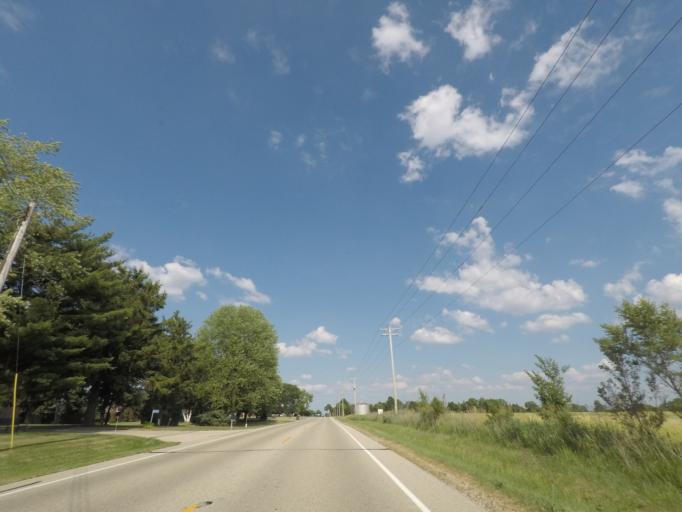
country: US
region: Wisconsin
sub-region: Walworth County
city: East Troy
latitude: 42.7929
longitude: -88.4737
